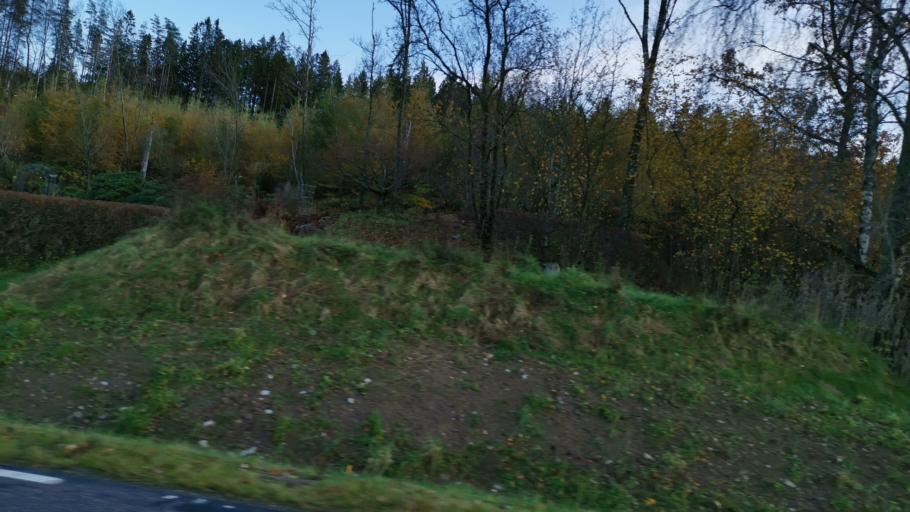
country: SE
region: Vaestra Goetaland
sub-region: Munkedals Kommun
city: Munkedal
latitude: 58.4892
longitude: 11.7109
